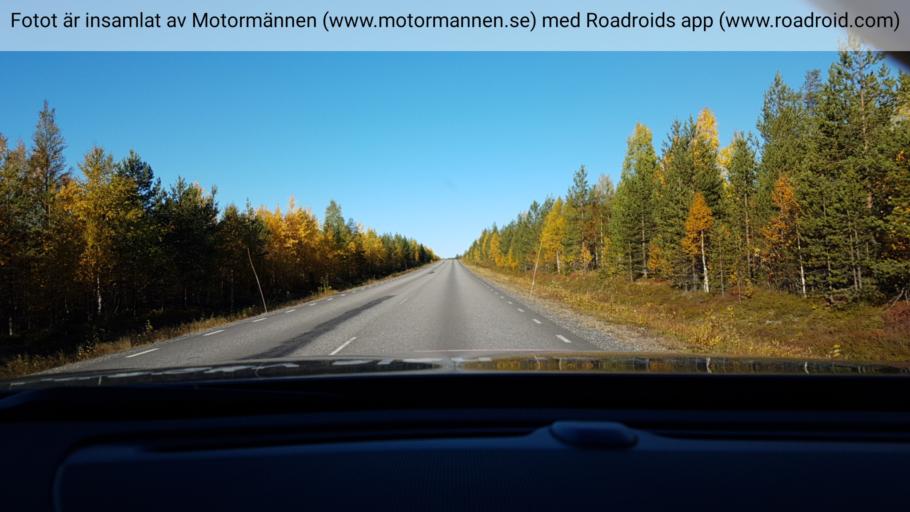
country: SE
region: Vaesterbotten
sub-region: Skelleftea Kommun
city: Storvik
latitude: 65.3260
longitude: 20.6880
